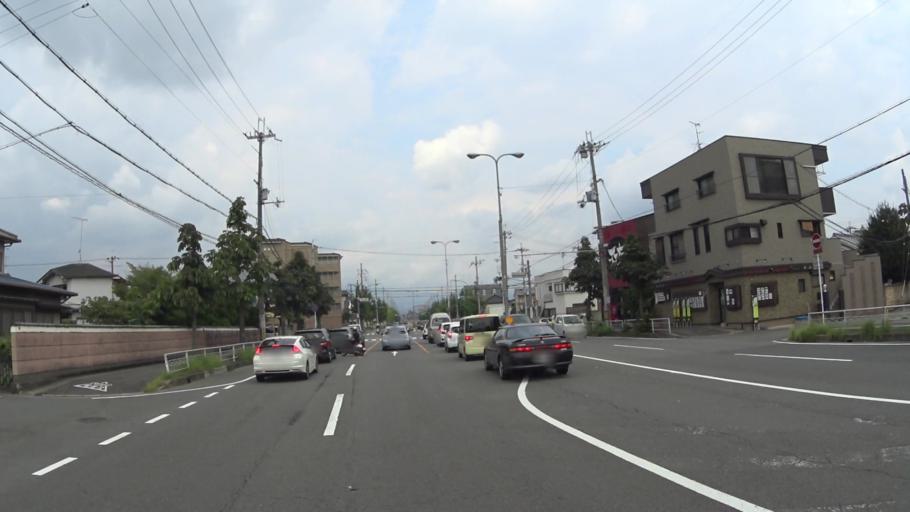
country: JP
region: Kyoto
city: Muko
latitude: 34.9886
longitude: 135.7049
